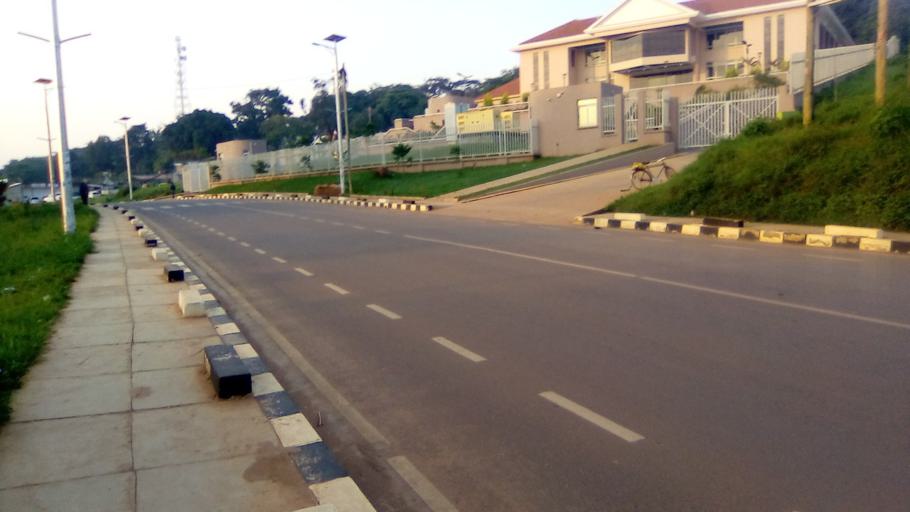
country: UG
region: Central Region
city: Masaka
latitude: -0.3388
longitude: 31.7376
